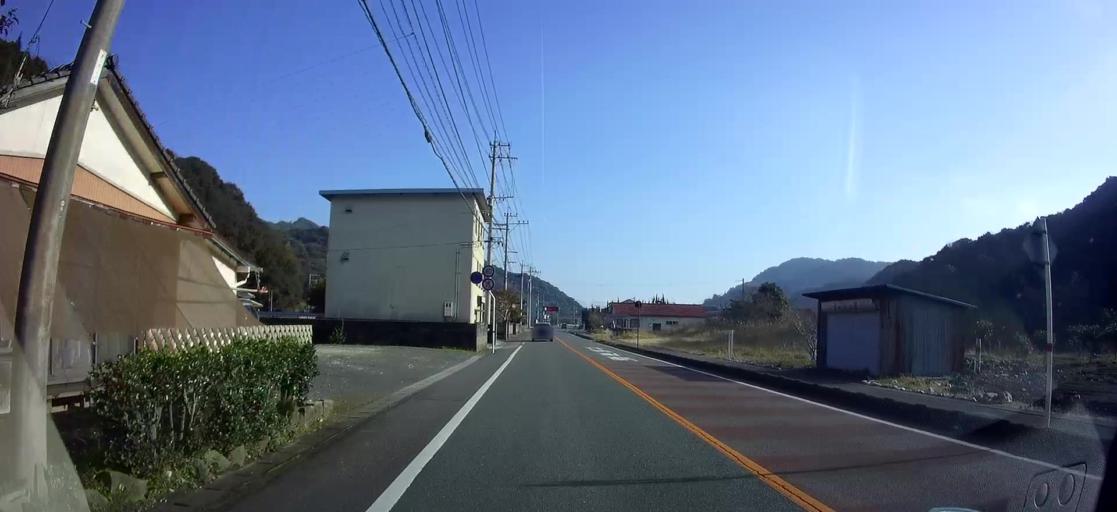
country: JP
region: Kumamoto
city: Hondo
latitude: 32.4305
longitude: 130.4003
